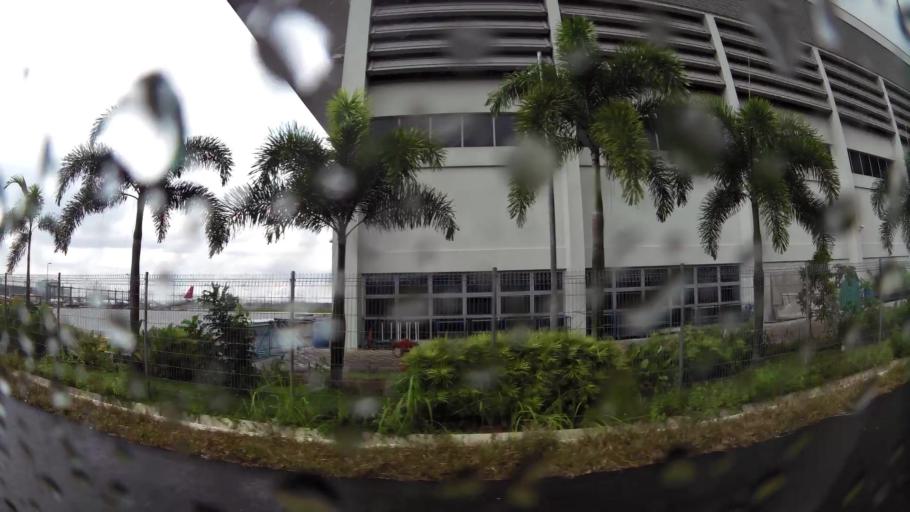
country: MY
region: Johor
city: Kampung Pasir Gudang Baru
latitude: 1.4106
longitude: 103.8676
